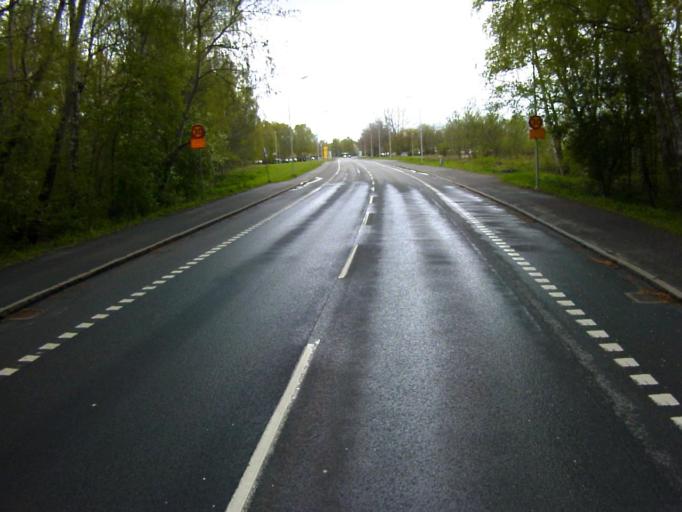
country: SE
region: Skane
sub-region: Kristianstads Kommun
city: Kristianstad
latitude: 56.0462
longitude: 14.1762
